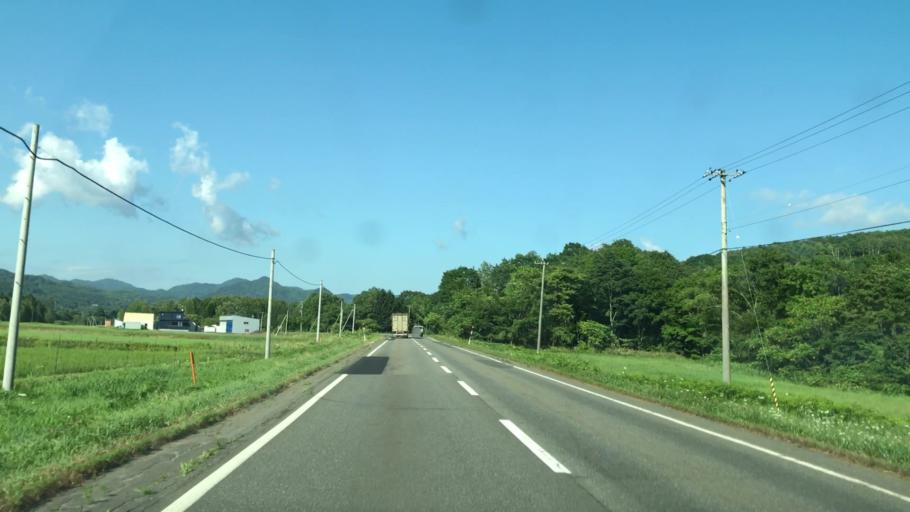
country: JP
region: Hokkaido
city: Shimo-furano
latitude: 42.8607
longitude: 142.4202
